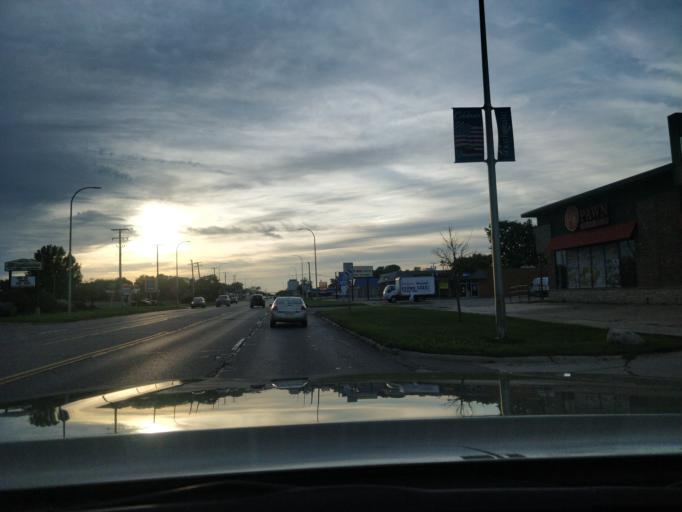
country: US
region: Michigan
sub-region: Wayne County
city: Southgate
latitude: 42.1989
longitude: -83.2194
